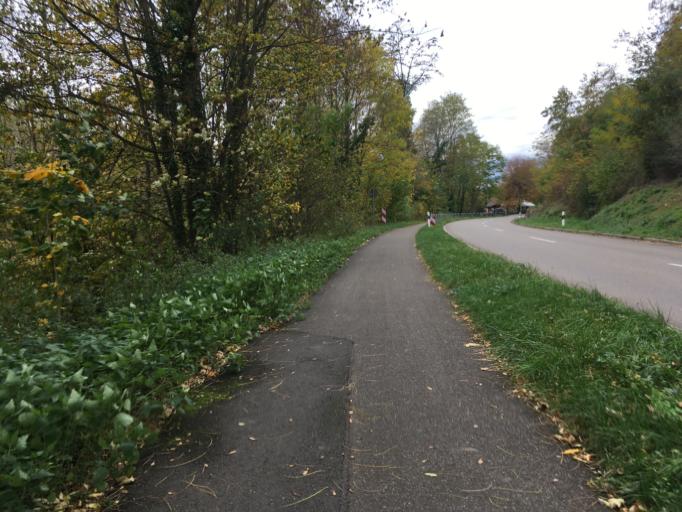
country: DE
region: Baden-Wuerttemberg
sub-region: Freiburg Region
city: Sasbach
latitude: 48.1457
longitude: 7.6035
